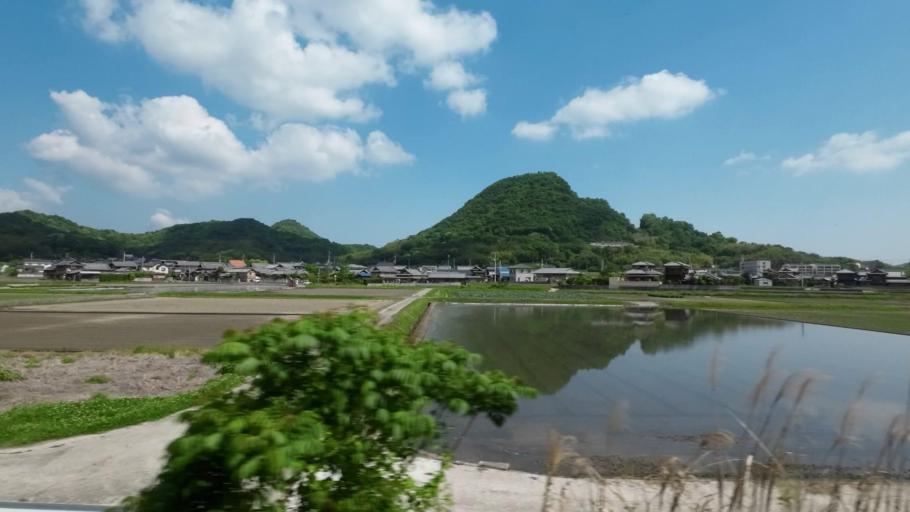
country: JP
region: Kagawa
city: Kan'onjicho
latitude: 34.1784
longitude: 133.7014
